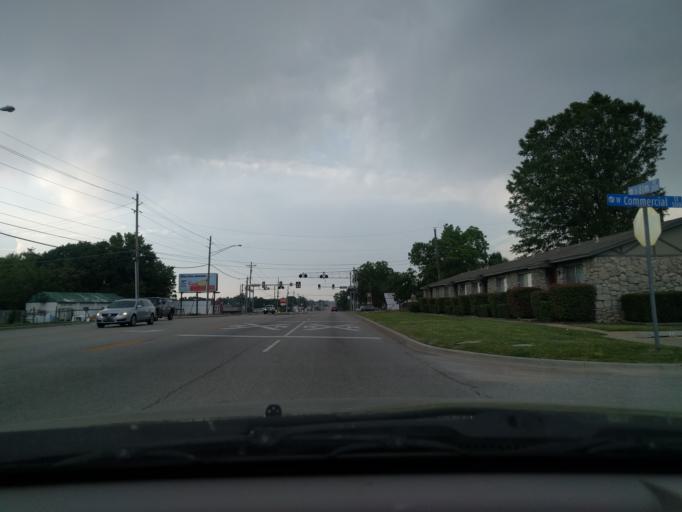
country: US
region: Oklahoma
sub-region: Tulsa County
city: Broken Arrow
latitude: 36.0513
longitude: -95.7974
